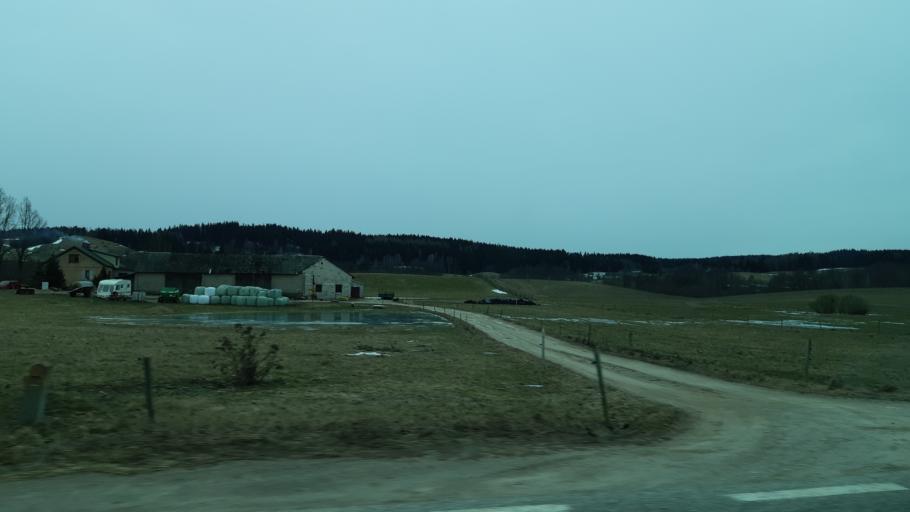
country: PL
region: Podlasie
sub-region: Suwalki
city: Suwalki
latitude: 54.3359
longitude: 22.9261
